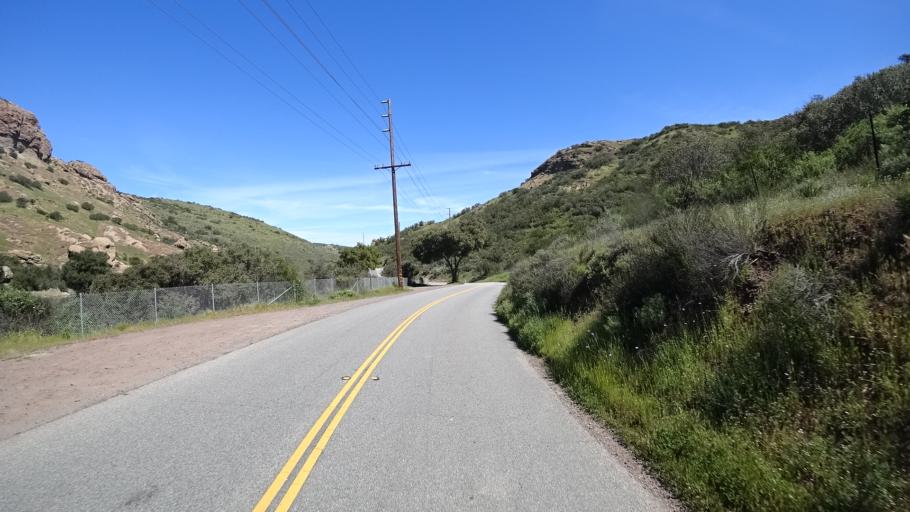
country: US
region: California
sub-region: Ventura County
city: Thousand Oaks
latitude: 34.1335
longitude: -118.8519
